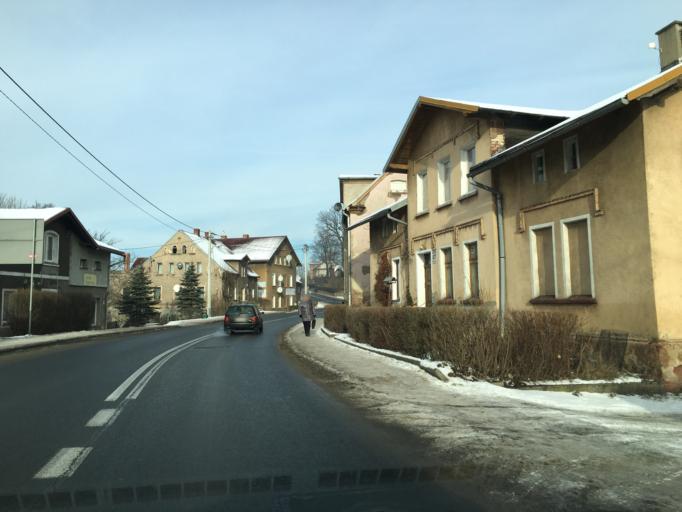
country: PL
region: Lower Silesian Voivodeship
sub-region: Powiat walbrzyski
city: Gluszyca Gorna
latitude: 50.6774
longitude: 16.3799
